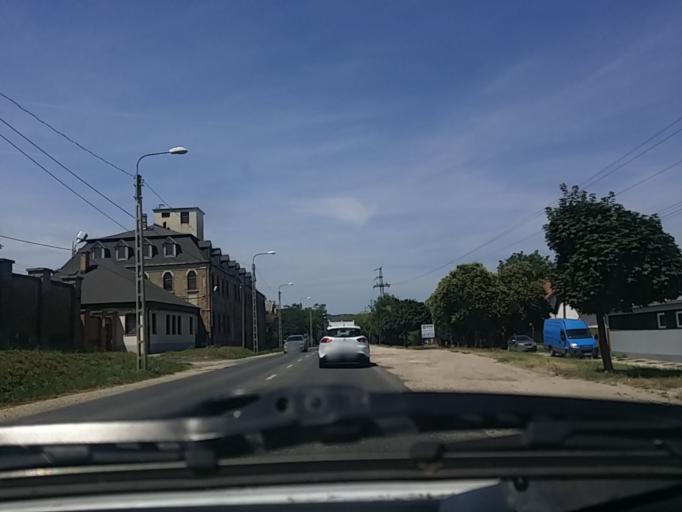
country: HU
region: Pest
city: Pilisvorosvar
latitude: 47.6148
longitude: 18.9234
